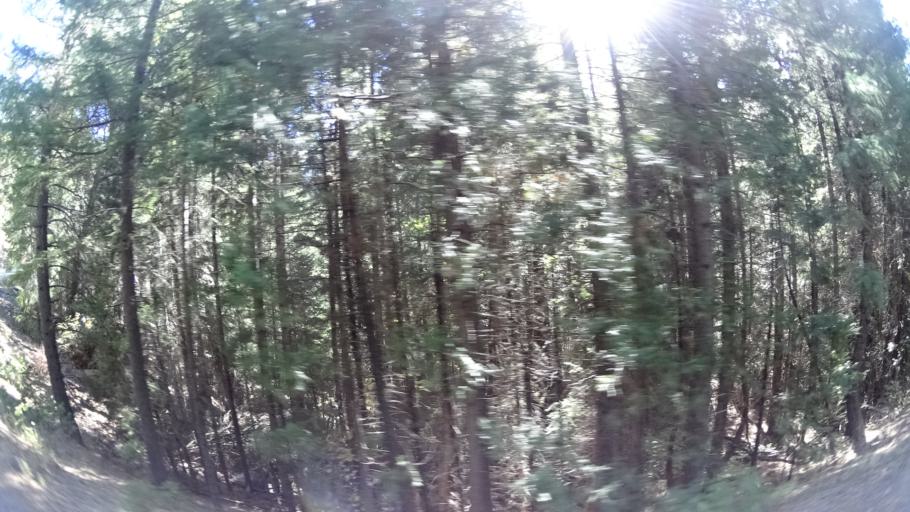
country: US
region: California
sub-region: Trinity County
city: Weaverville
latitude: 41.2214
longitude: -123.0220
